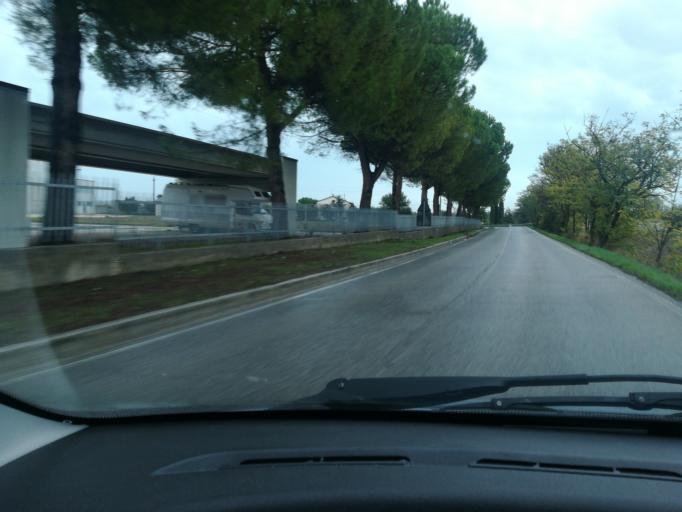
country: IT
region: The Marches
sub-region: Provincia di Macerata
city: Trodica
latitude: 43.2762
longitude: 13.6053
